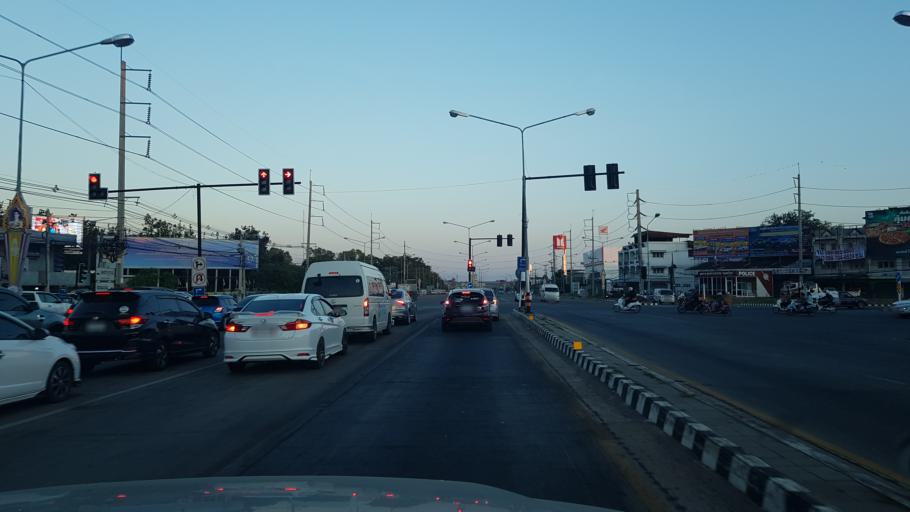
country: TH
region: Khon Kaen
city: Chum Phae
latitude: 16.5414
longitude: 102.1079
